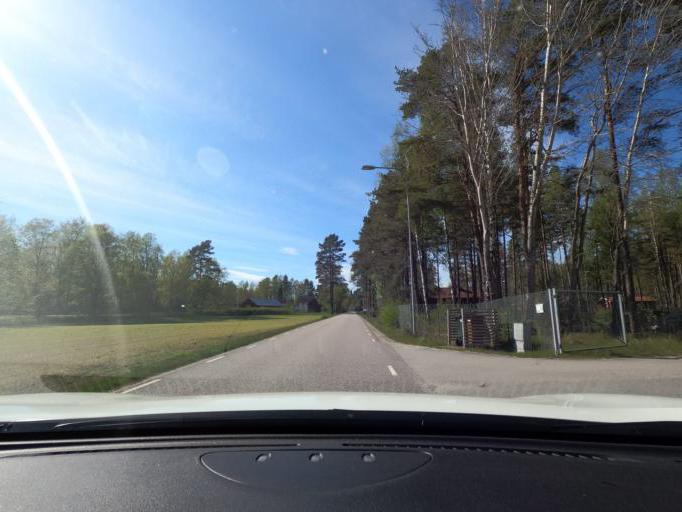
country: SE
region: Vaestra Goetaland
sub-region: Harryda Kommun
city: Ravlanda
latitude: 57.6469
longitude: 12.4953
